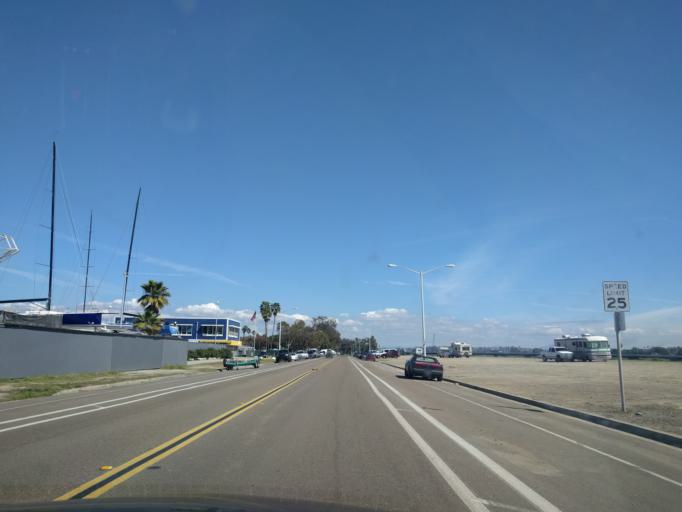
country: US
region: California
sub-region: San Diego County
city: Coronado
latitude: 32.7586
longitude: -117.2403
